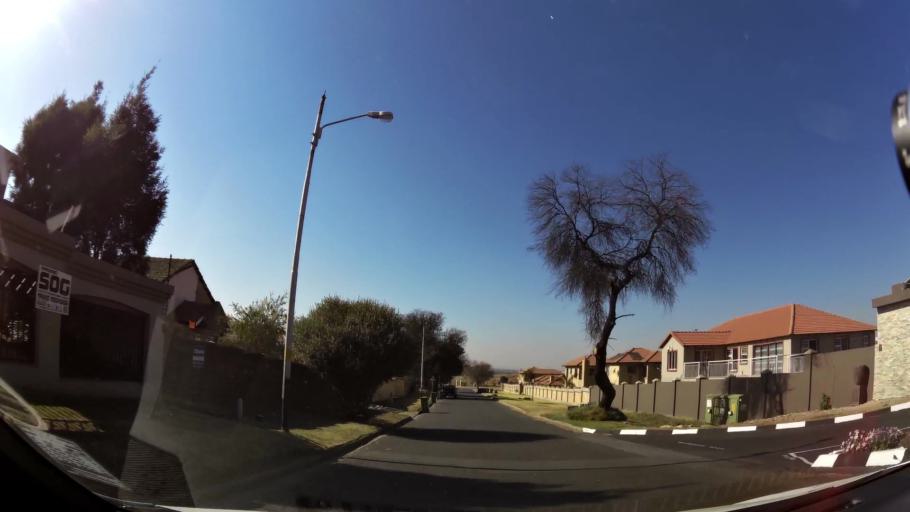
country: ZA
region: Gauteng
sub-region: Ekurhuleni Metropolitan Municipality
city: Germiston
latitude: -26.2559
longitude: 28.1115
